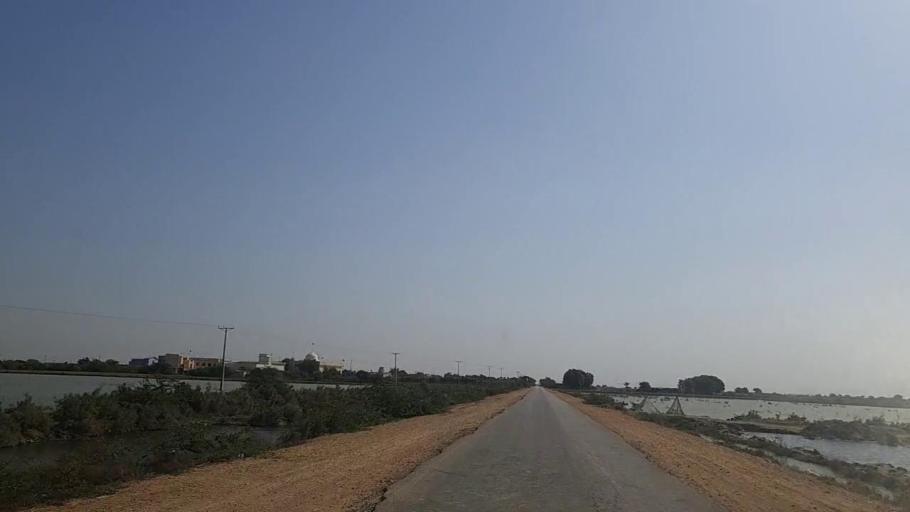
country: PK
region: Sindh
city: Mirpur Batoro
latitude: 24.6439
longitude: 68.2900
